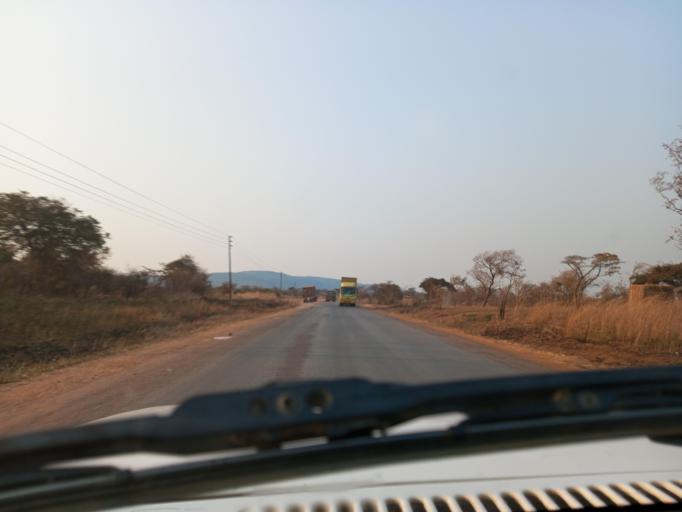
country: ZM
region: Northern
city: Mpika
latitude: -11.9257
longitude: 31.4176
